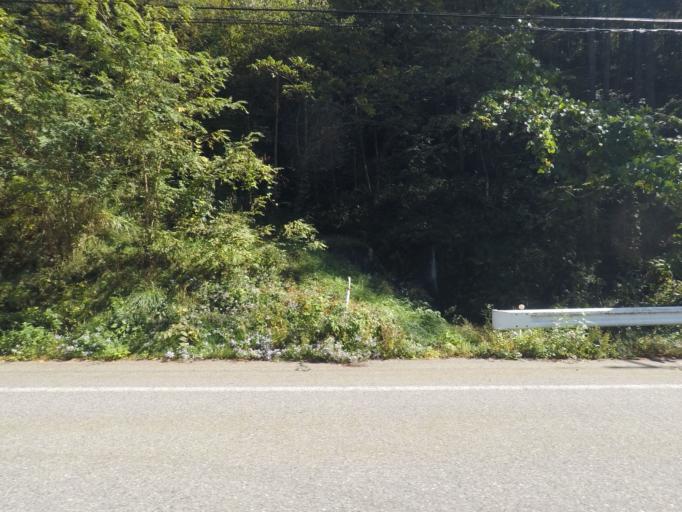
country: JP
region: Nagano
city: Shiojiri
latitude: 35.9977
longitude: 137.7385
